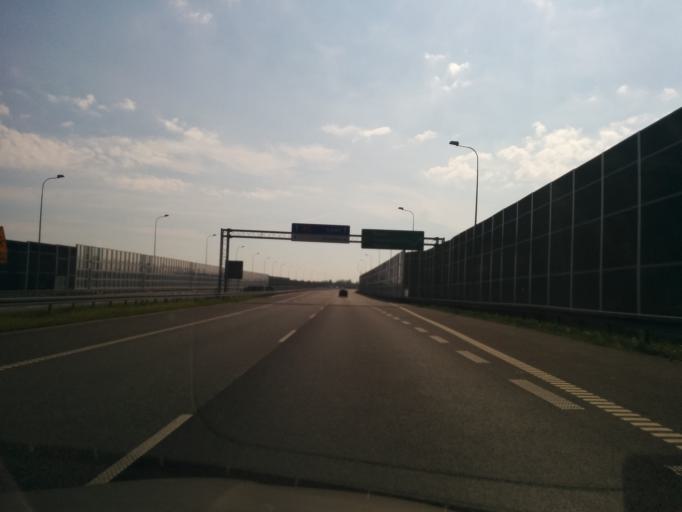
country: PL
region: Silesian Voivodeship
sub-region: Powiat tarnogorski
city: Radzionkow
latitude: 50.3725
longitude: 18.8899
